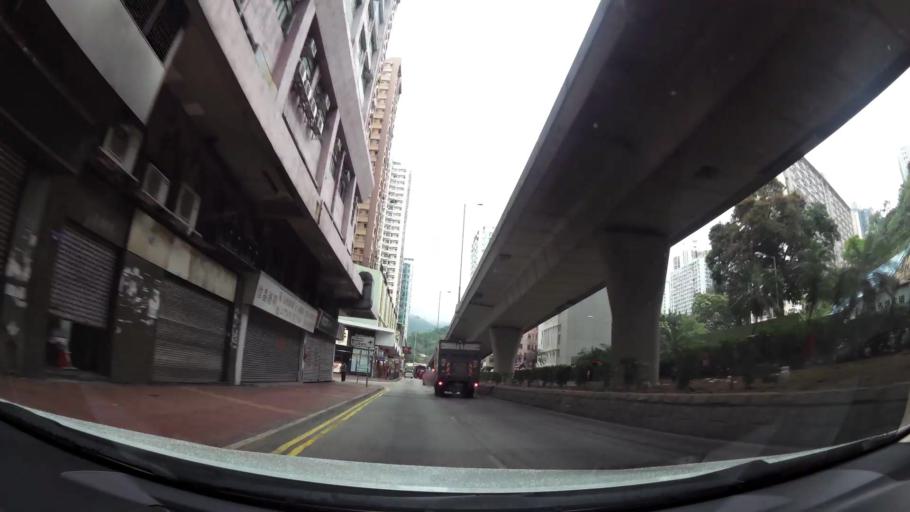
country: HK
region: Tsuen Wan
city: Tsuen Wan
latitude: 22.3677
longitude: 114.1218
